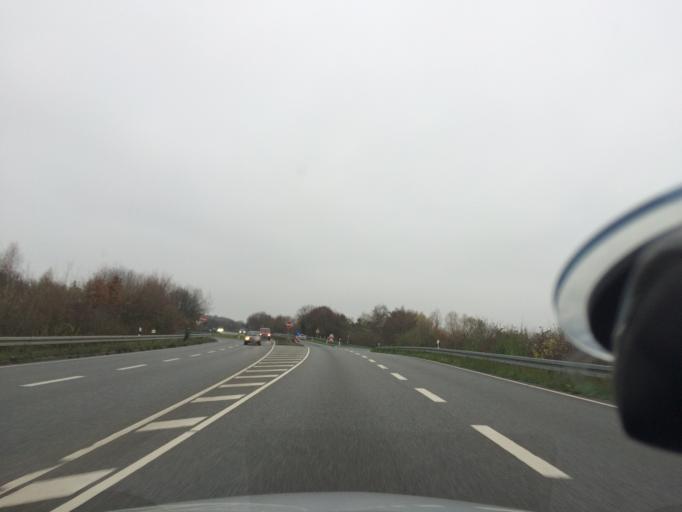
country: DE
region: Hesse
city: Langen
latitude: 49.9963
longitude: 8.6769
